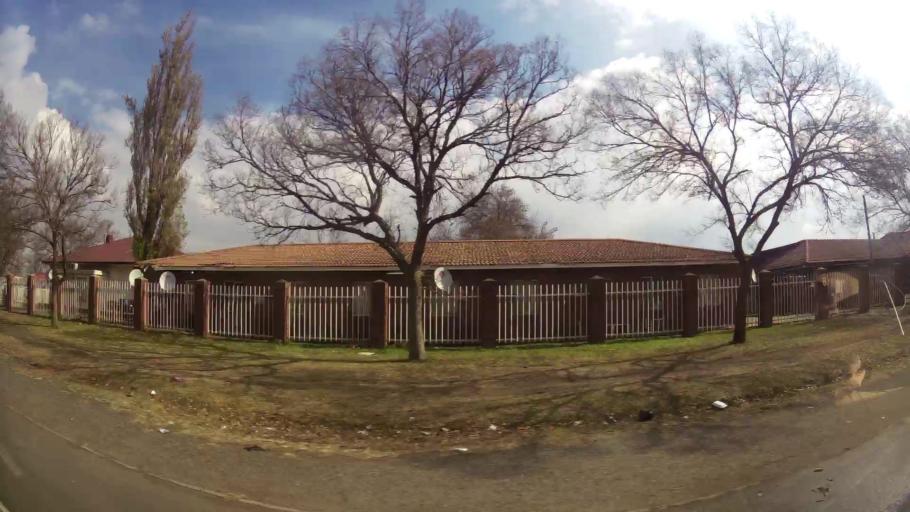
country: ZA
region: Gauteng
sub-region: Sedibeng District Municipality
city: Vereeniging
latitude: -26.6677
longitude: 27.9244
